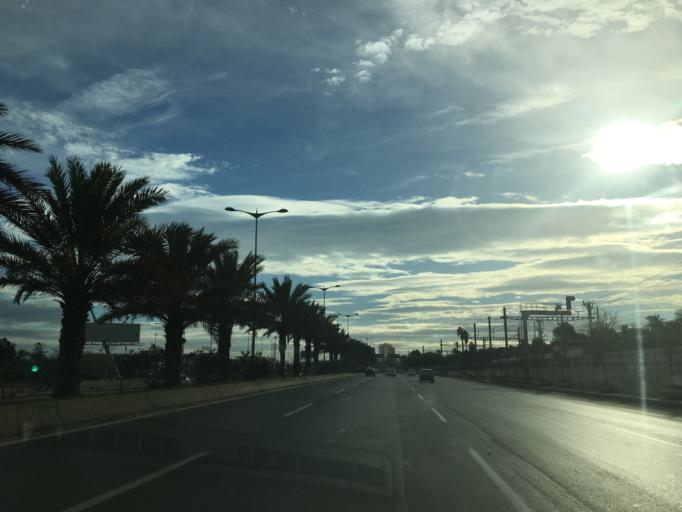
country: DZ
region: Alger
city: Algiers
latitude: 36.7531
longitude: 3.0728
